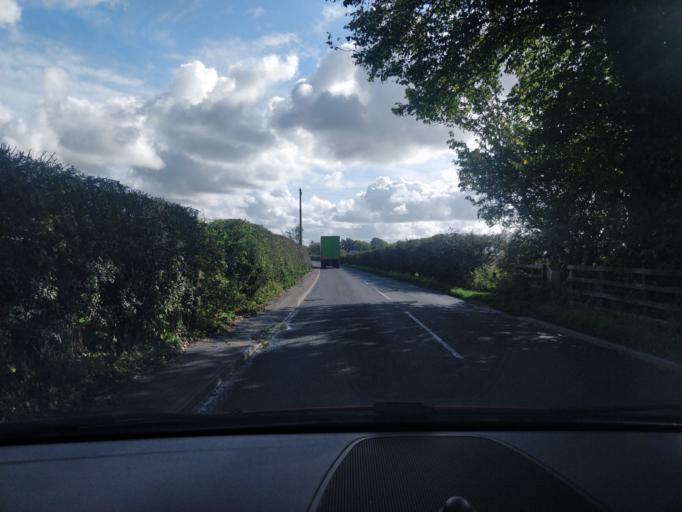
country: GB
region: England
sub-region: Lancashire
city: Ormskirk
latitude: 53.5948
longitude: -2.8940
